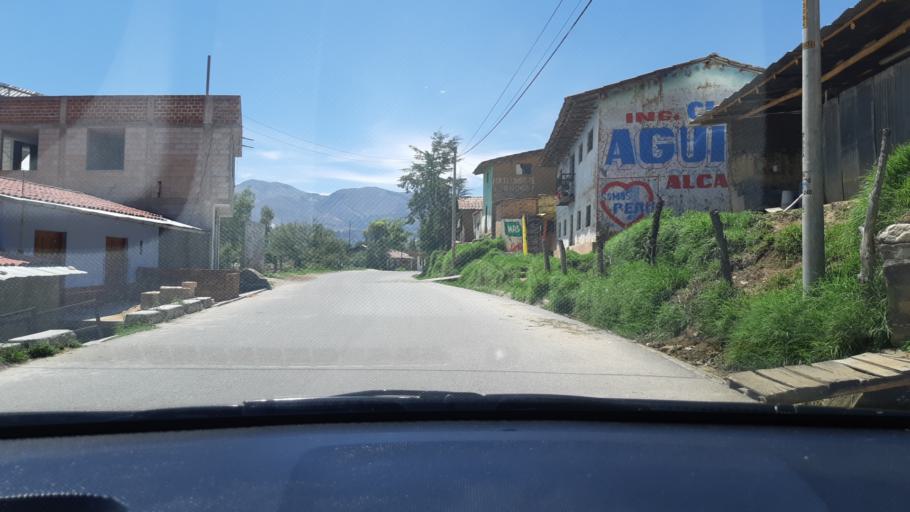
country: PE
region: Cajamarca
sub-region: Provincia de Cajamarca
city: Llacanora
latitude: -7.1817
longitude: -78.4513
